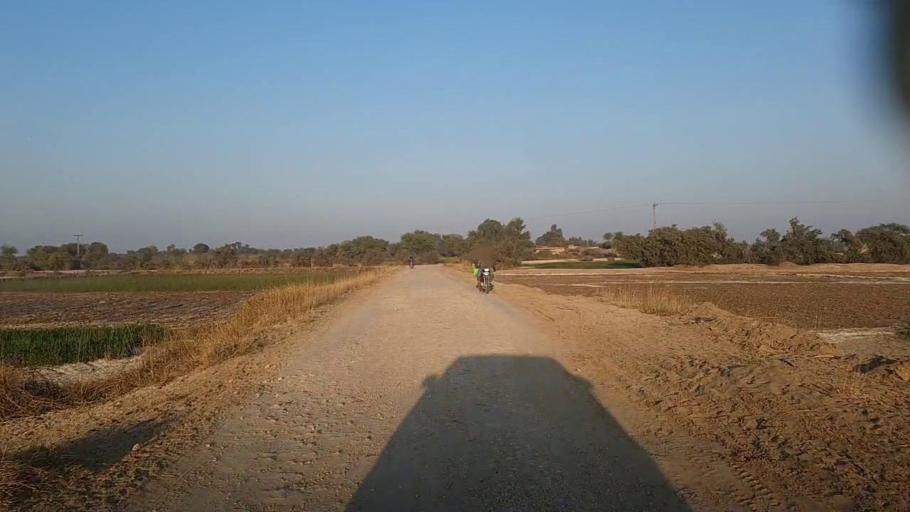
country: PK
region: Sindh
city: Mirpur Mathelo
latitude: 27.8903
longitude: 69.6576
